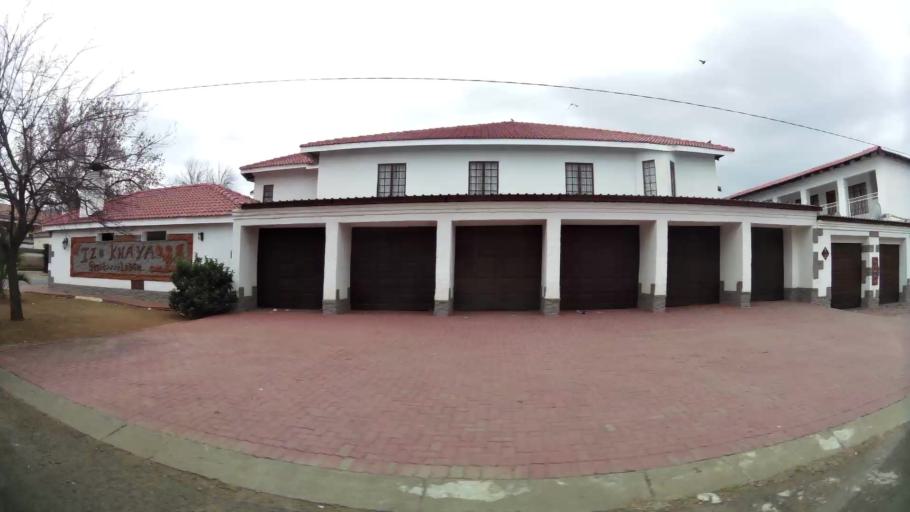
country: ZA
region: Orange Free State
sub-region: Fezile Dabi District Municipality
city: Kroonstad
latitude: -27.6575
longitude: 27.2416
